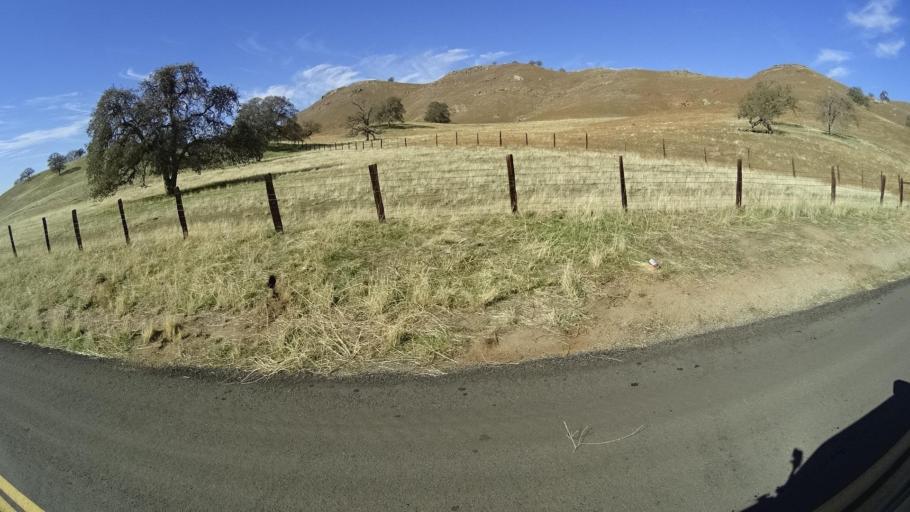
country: US
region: California
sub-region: Tulare County
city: Richgrove
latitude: 35.6844
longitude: -118.8424
